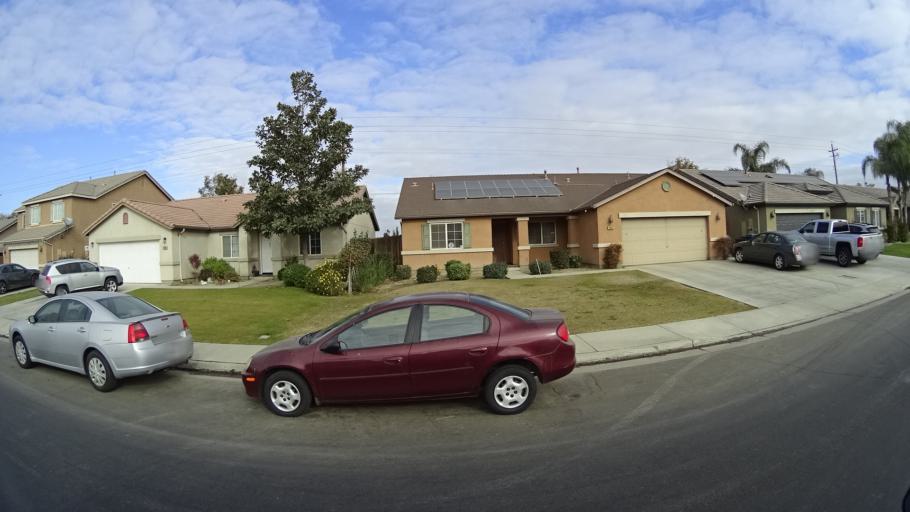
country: US
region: California
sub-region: Kern County
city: Rosedale
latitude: 35.3029
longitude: -119.1351
